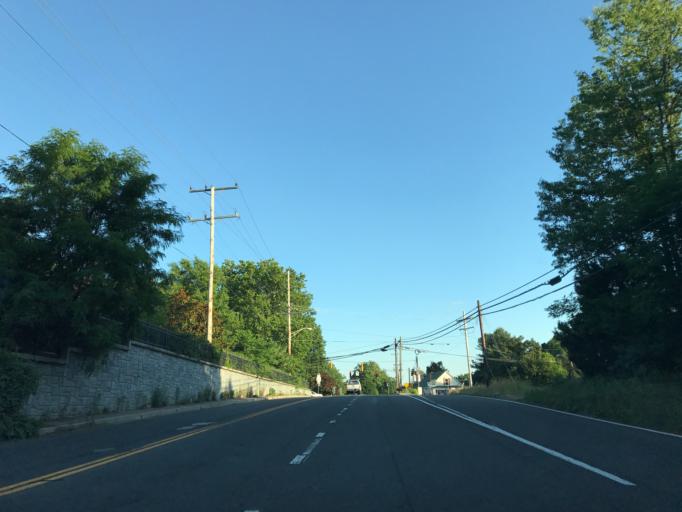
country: US
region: Maryland
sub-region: Anne Arundel County
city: Davidsonville
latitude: 38.9240
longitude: -76.6286
